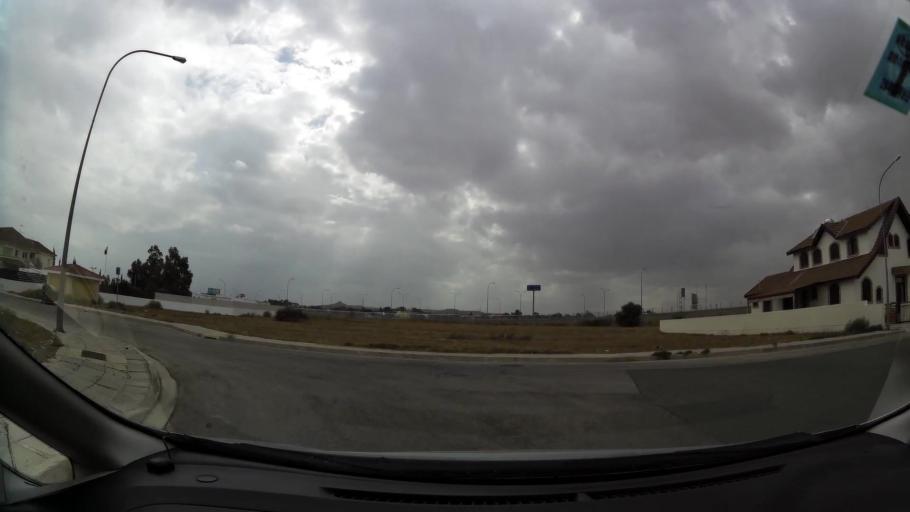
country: CY
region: Lefkosia
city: Geri
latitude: 35.1118
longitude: 33.3673
